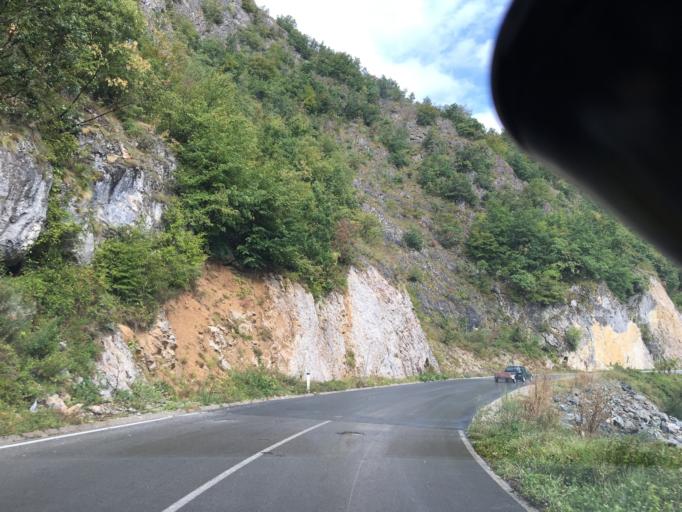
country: ME
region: Berane
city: Berane
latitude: 42.8298
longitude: 19.8357
